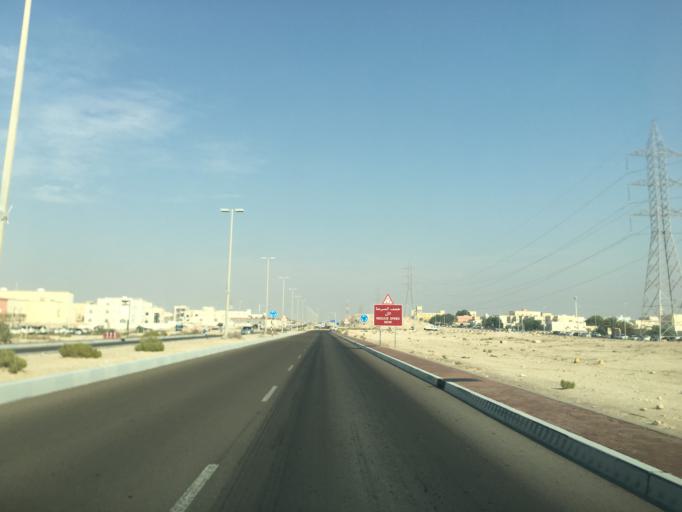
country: AE
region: Abu Dhabi
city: Abu Dhabi
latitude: 24.3018
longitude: 54.6544
